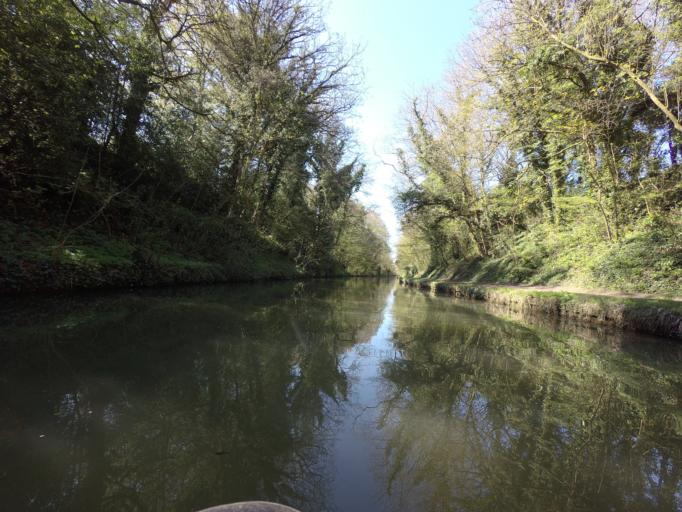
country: GB
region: England
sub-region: Hertfordshire
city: Tring
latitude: 51.8019
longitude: -0.6341
